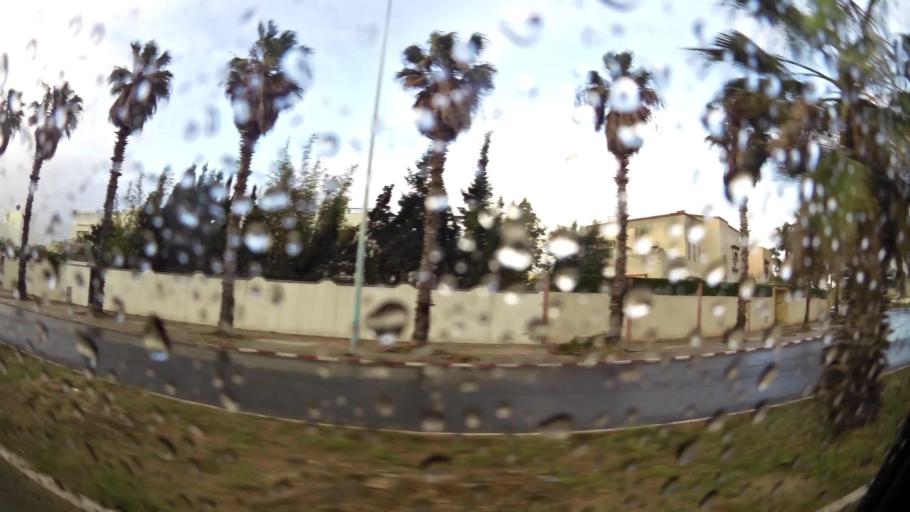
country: MA
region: Doukkala-Abda
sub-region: El-Jadida
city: El Jadida
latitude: 33.2406
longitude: -8.5093
